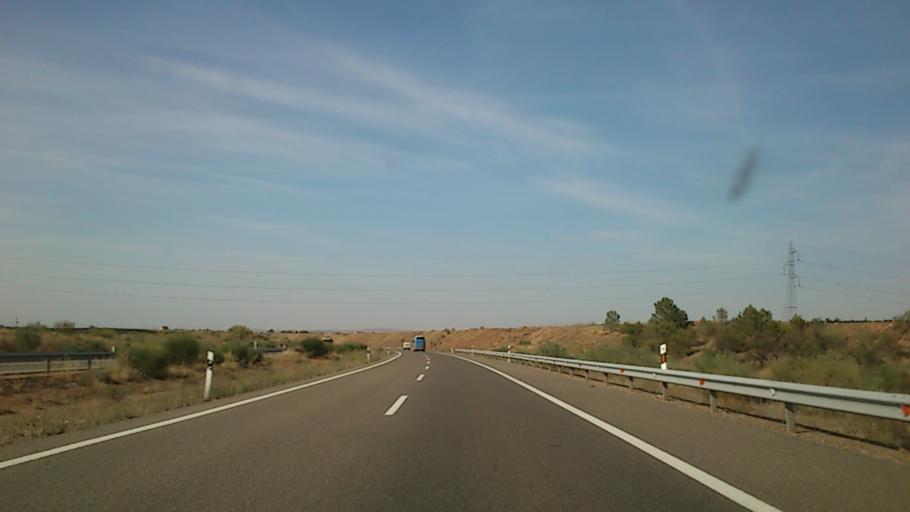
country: ES
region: Aragon
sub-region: Provincia de Zaragoza
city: Carinena
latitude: 41.3255
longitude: -1.2034
